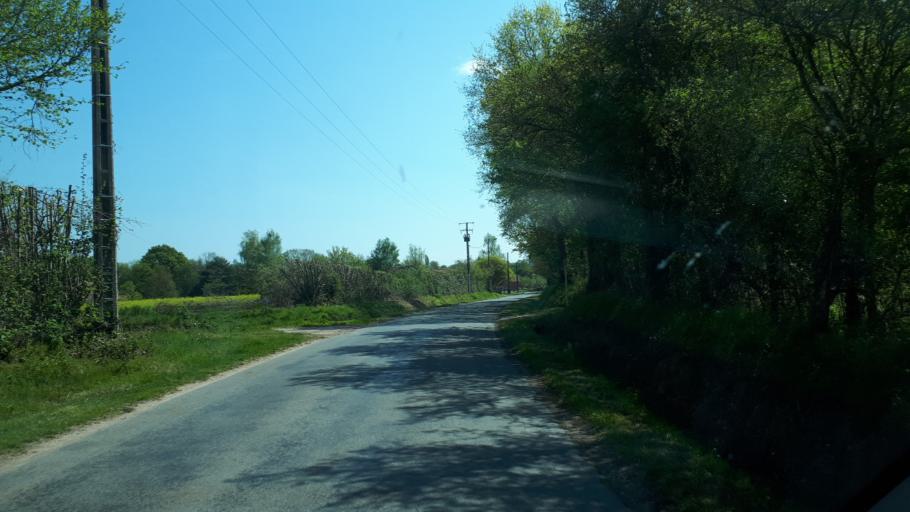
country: FR
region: Centre
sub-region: Departement du Cher
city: Neuvy-sur-Barangeon
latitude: 47.3155
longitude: 2.3549
